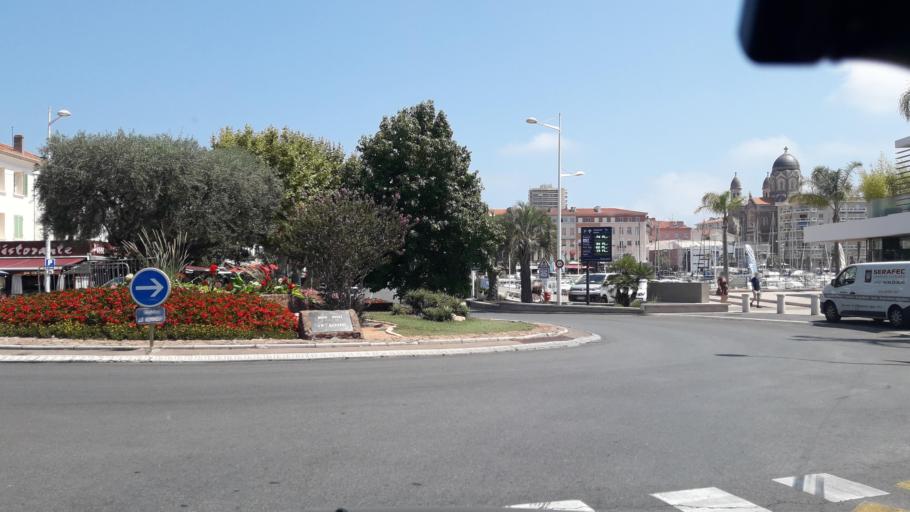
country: FR
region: Provence-Alpes-Cote d'Azur
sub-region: Departement du Var
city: Saint-Raphael
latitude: 43.4244
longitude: 6.7640
